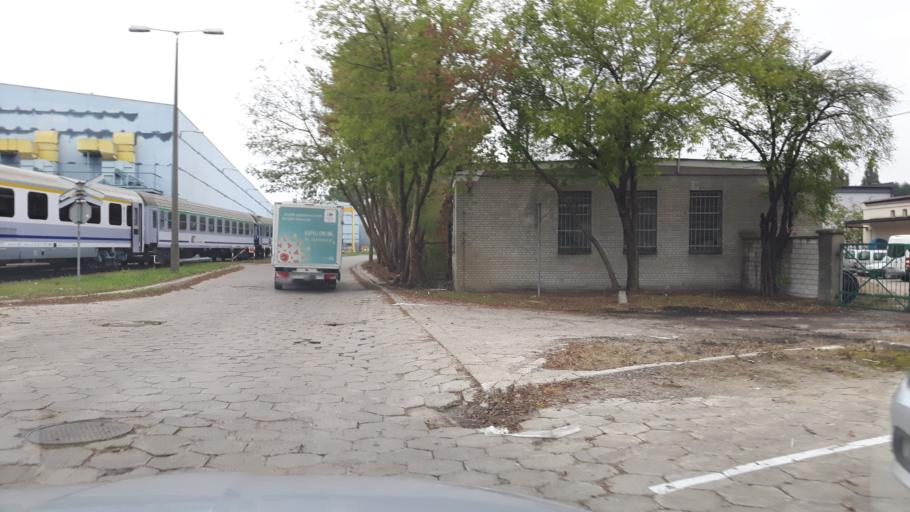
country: PL
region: Masovian Voivodeship
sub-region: Warszawa
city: Praga Poludnie
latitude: 52.2512
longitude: 21.1124
